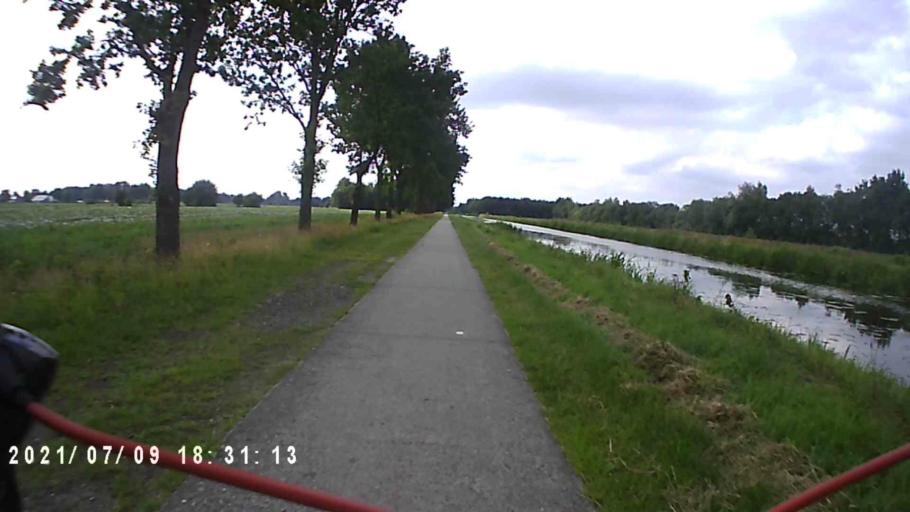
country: NL
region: Groningen
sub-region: Gemeente Pekela
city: Oude Pekela
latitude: 53.0675
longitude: 6.9746
